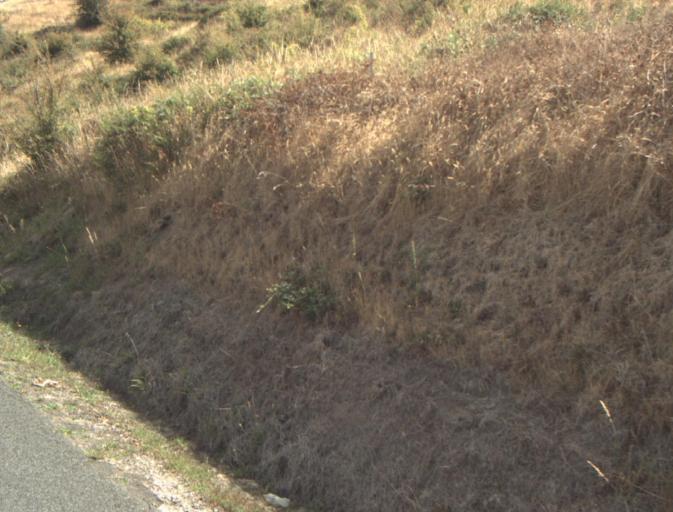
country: AU
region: Tasmania
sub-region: Launceston
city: Mayfield
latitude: -41.2412
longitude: 147.1493
